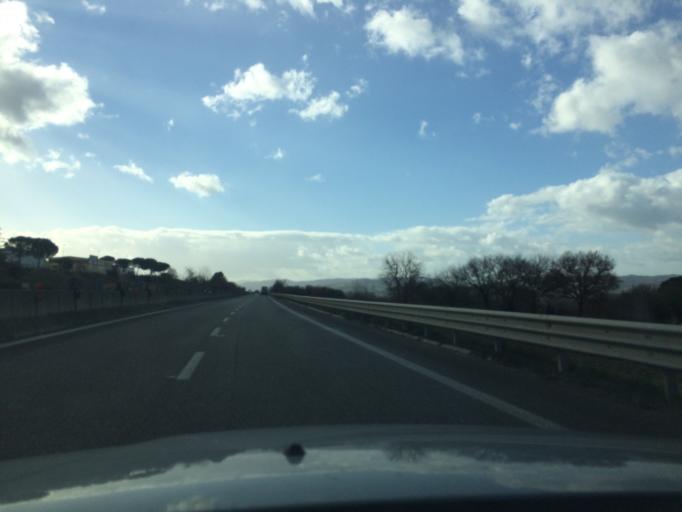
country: IT
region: Umbria
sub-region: Provincia di Perugia
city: Collepepe
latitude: 42.9078
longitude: 12.3918
